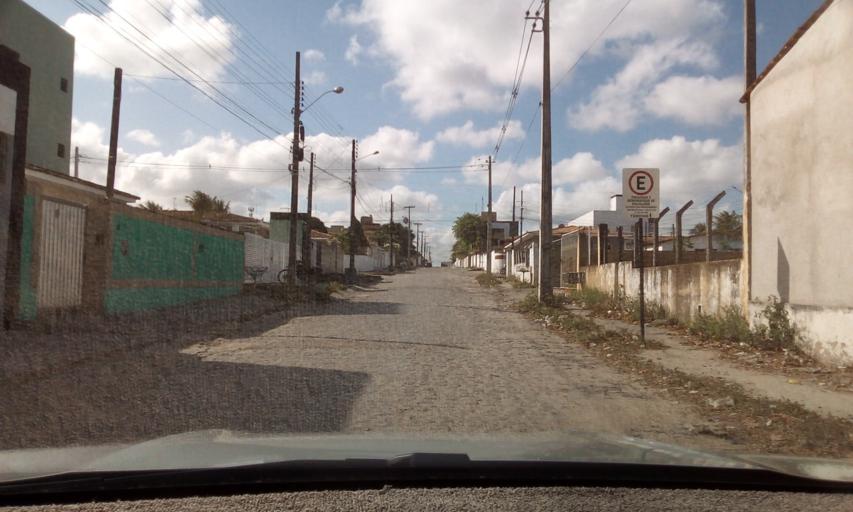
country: BR
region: Paraiba
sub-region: Bayeux
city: Bayeux
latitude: -7.1789
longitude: -34.9152
